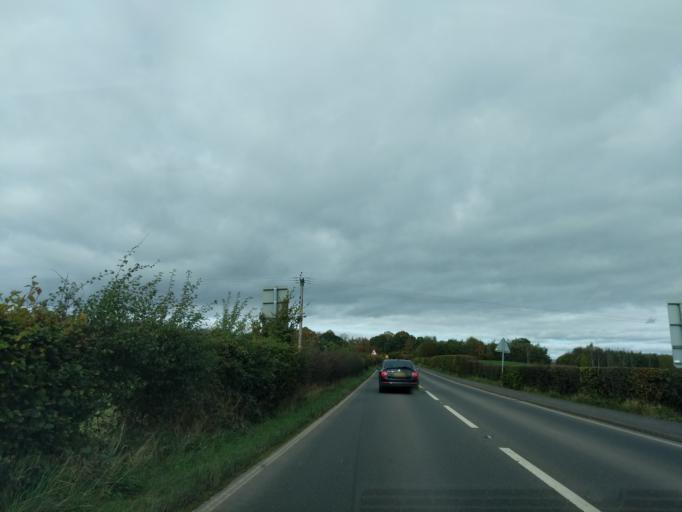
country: GB
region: Scotland
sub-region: Dumfries and Galloway
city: Thornhill
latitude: 55.2462
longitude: -3.7709
